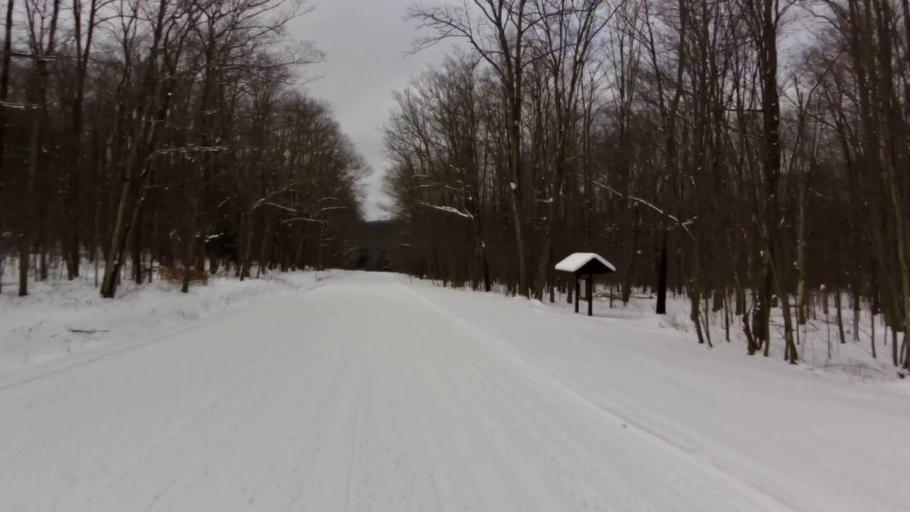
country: US
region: New York
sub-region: Cattaraugus County
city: Salamanca
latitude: 42.0345
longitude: -78.7979
